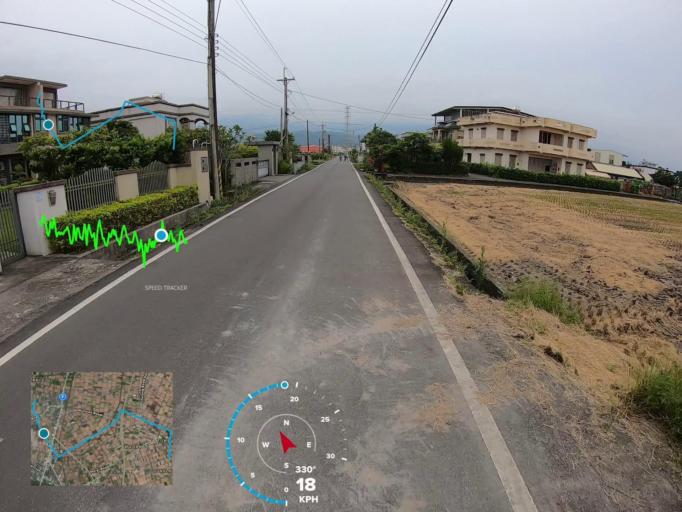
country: TW
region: Taiwan
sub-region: Yilan
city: Yilan
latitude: 24.7801
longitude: 121.7635
